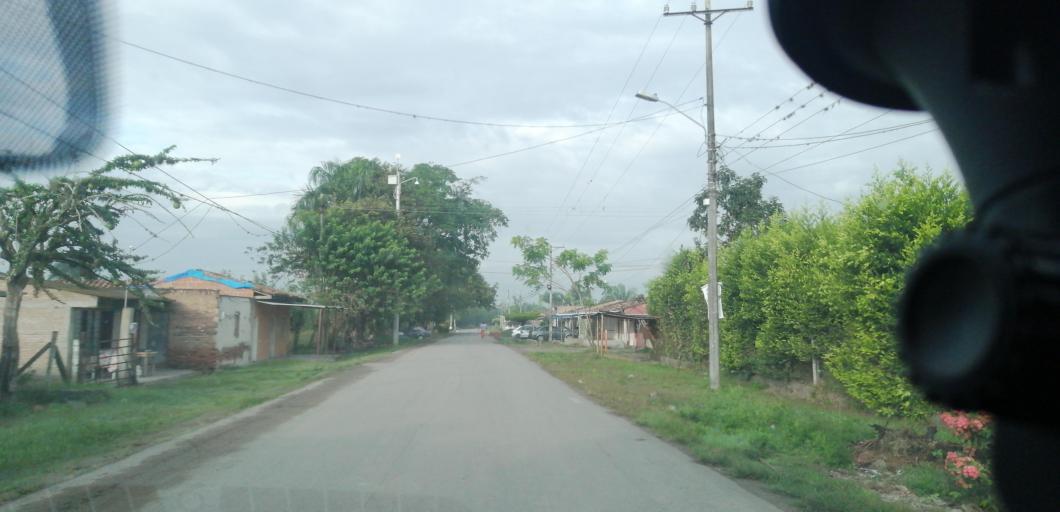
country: CO
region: Valle del Cauca
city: Palmira
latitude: 3.5368
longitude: -76.3523
